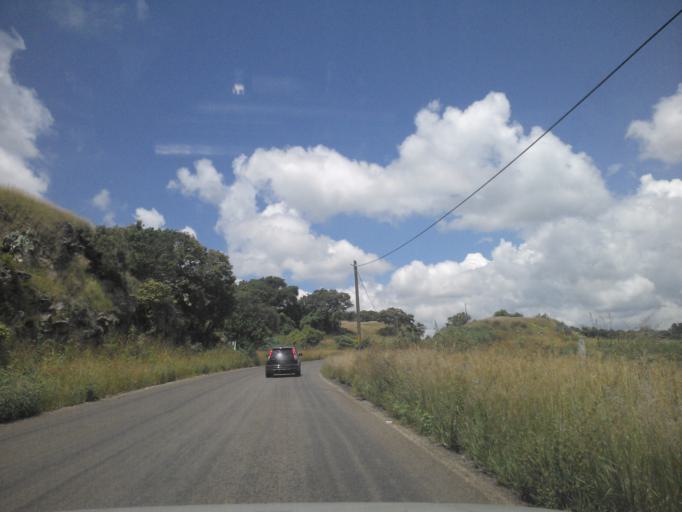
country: MX
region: Jalisco
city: Atotonilco el Alto
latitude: 20.5641
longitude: -102.4957
